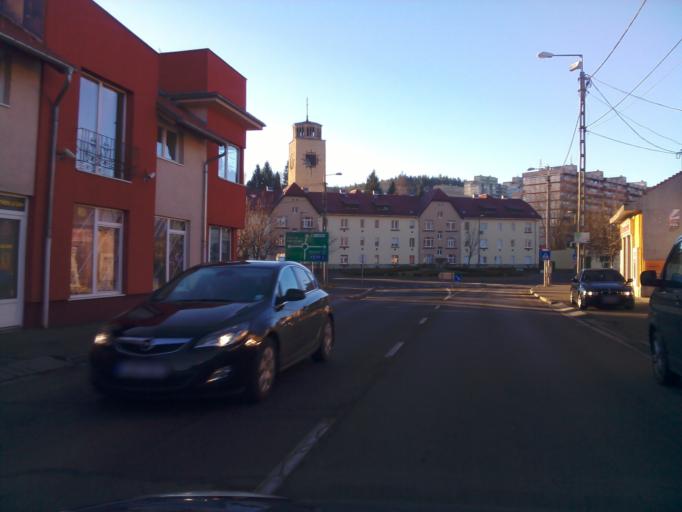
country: HU
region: Nograd
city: Salgotarjan
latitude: 48.1100
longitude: 19.8118
